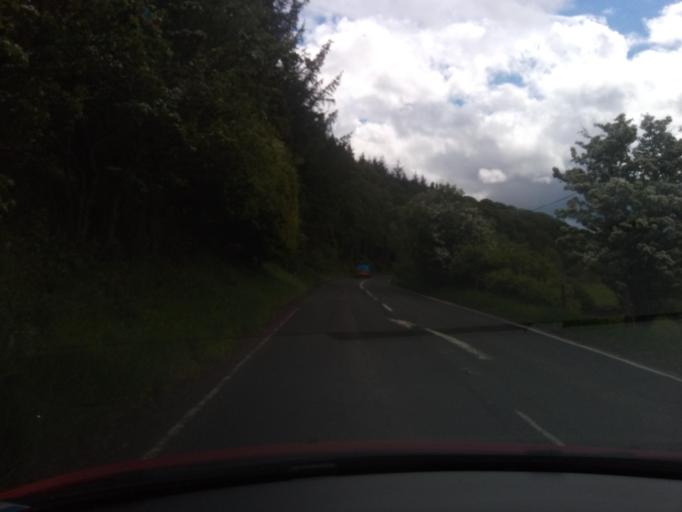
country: GB
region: Scotland
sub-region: The Scottish Borders
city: Galashiels
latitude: 55.6883
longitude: -2.8631
